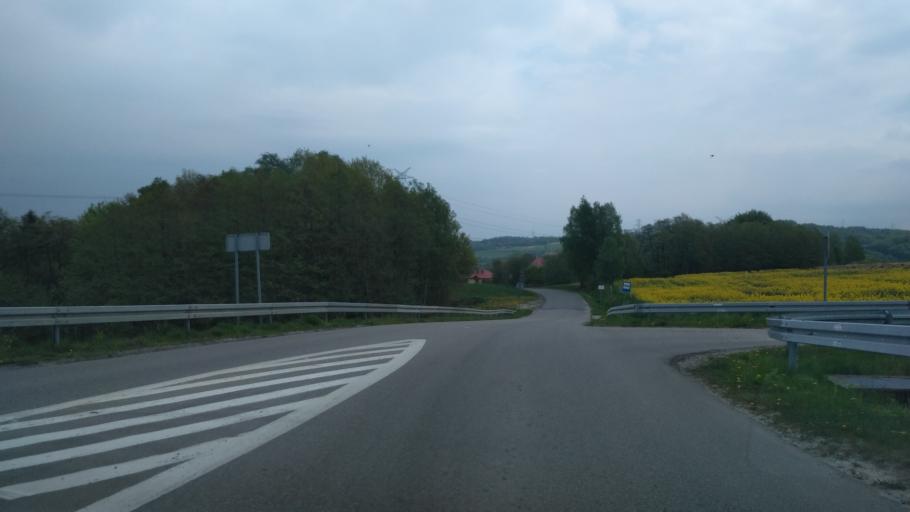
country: PL
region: Lesser Poland Voivodeship
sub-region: Powiat tarnowski
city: Tarnowiec
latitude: 49.9451
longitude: 21.0153
